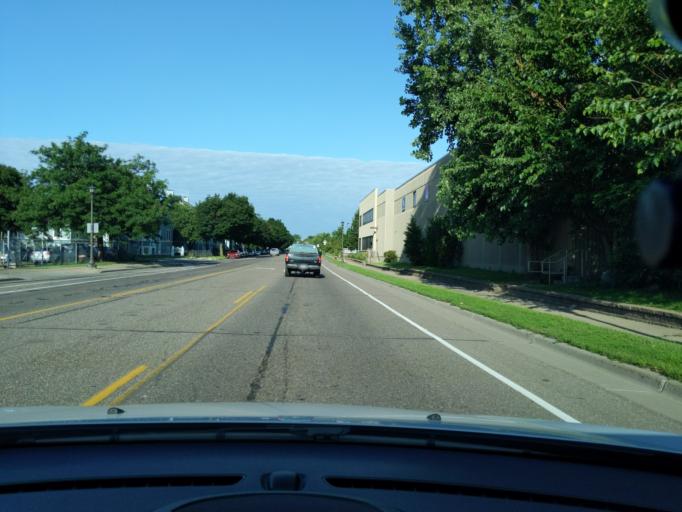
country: US
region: Minnesota
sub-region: Ramsey County
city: Saint Paul
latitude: 44.9630
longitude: -93.1204
